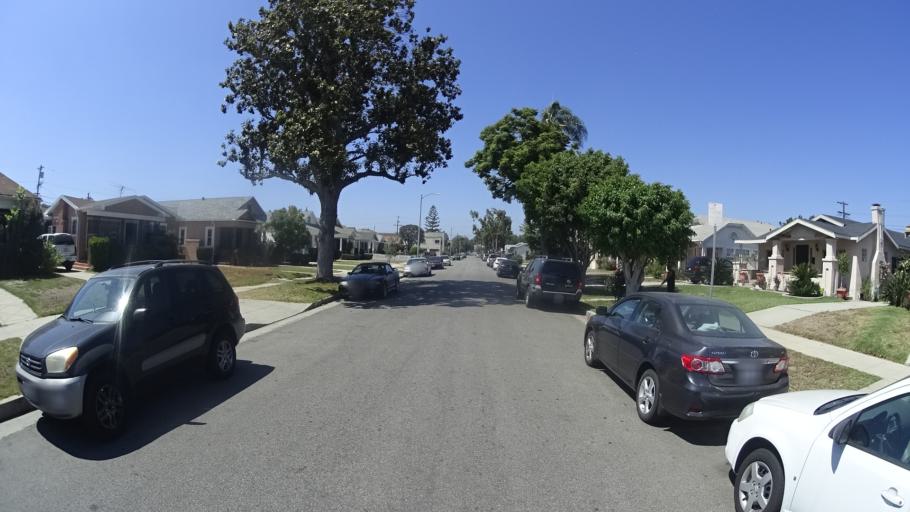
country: US
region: California
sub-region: Los Angeles County
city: View Park-Windsor Hills
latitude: 34.0062
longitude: -118.2988
